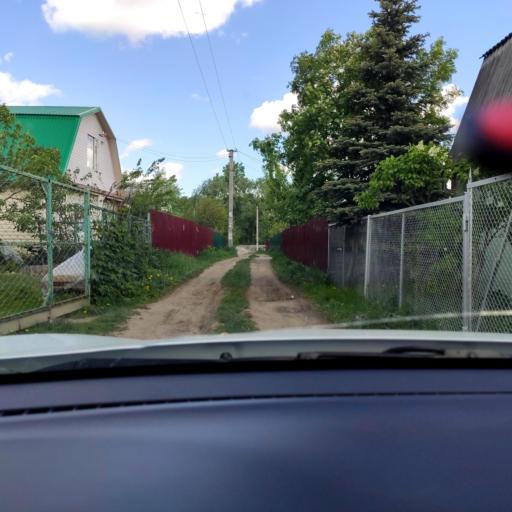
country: RU
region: Tatarstan
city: Stolbishchi
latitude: 55.6990
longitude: 49.1812
